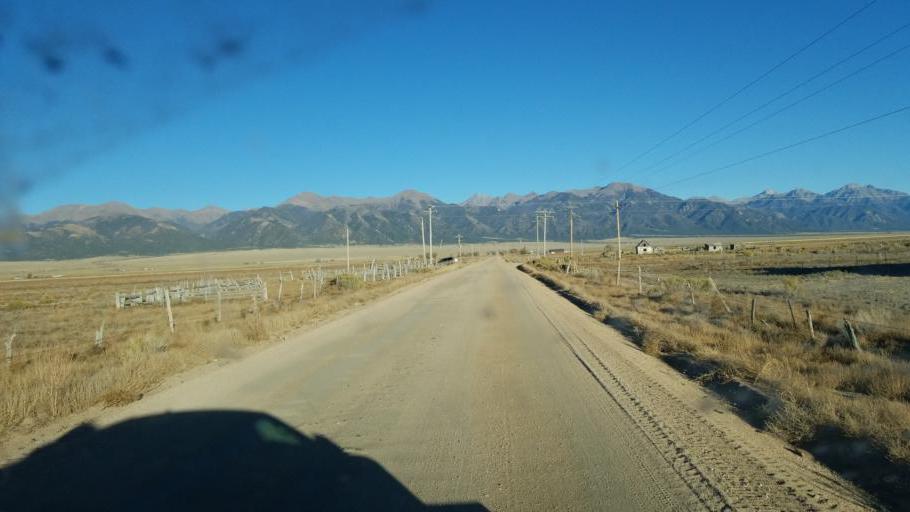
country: US
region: Colorado
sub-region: Saguache County
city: Saguache
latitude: 38.1003
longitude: -105.9045
